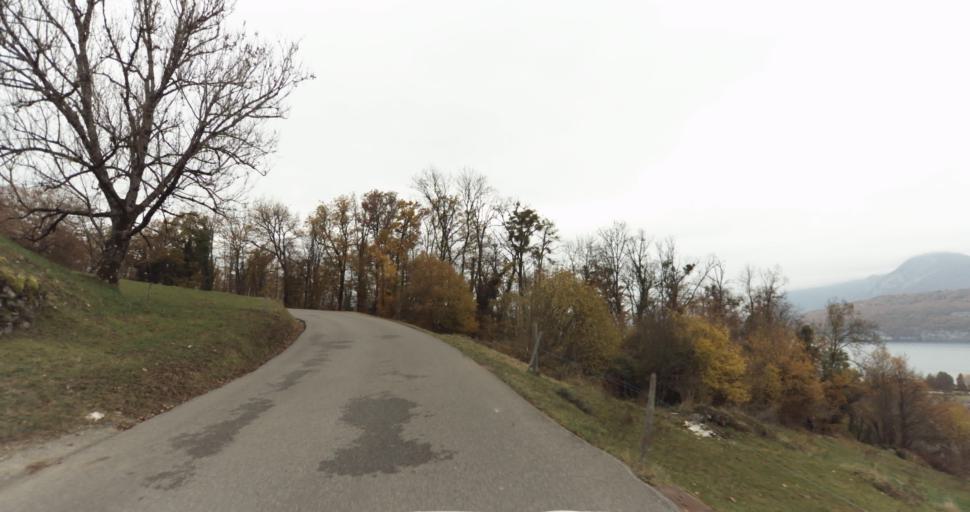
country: FR
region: Rhone-Alpes
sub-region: Departement de la Haute-Savoie
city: Talloires
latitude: 45.8217
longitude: 6.1972
